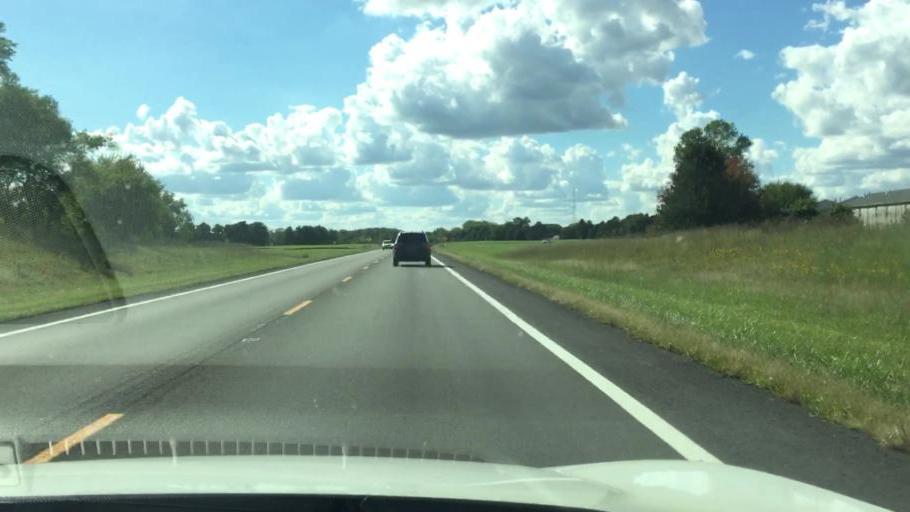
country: US
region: Ohio
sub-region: Clark County
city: Northridge
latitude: 39.9772
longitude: -83.7600
